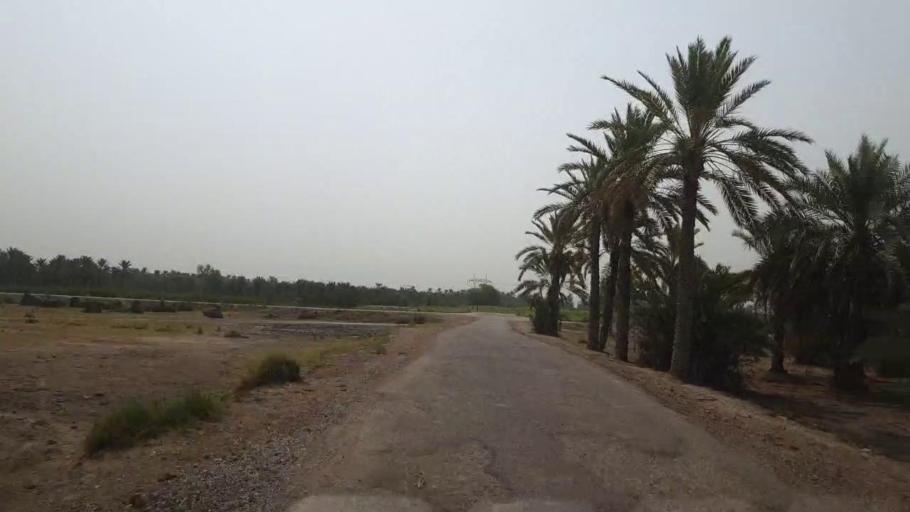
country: PK
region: Sindh
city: Gambat
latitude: 27.4156
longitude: 68.5509
